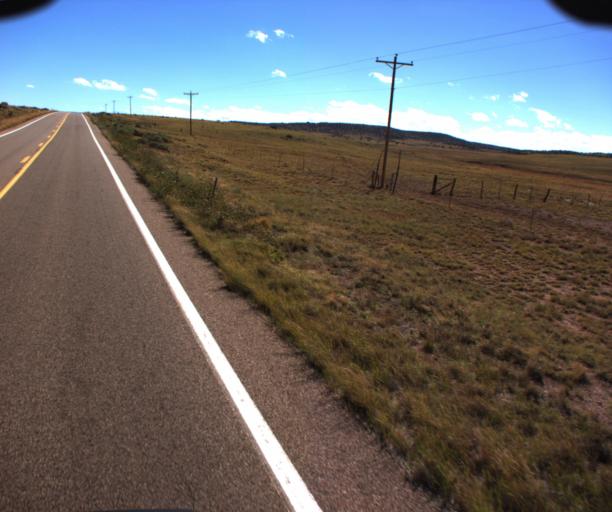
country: US
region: Arizona
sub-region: Apache County
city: Saint Johns
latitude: 34.4926
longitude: -109.6212
